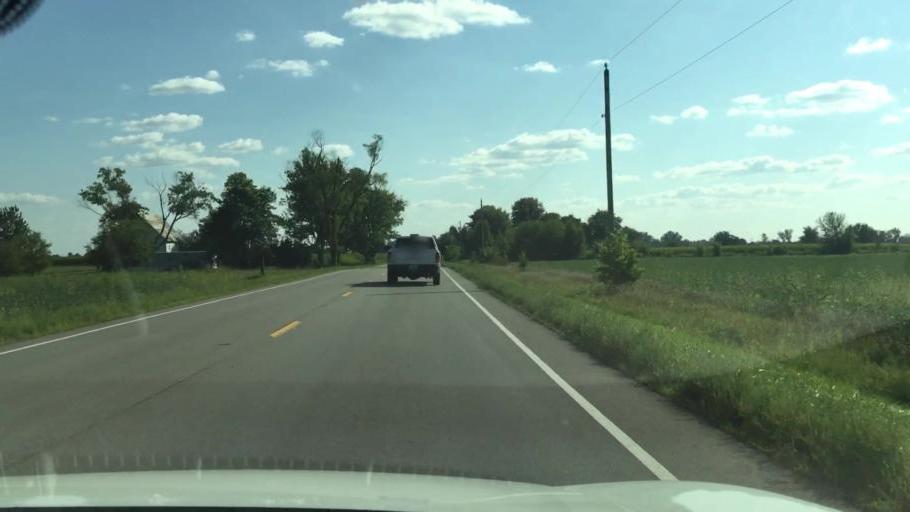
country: US
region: Ohio
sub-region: Champaign County
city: Mechanicsburg
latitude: 40.1342
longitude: -83.4829
